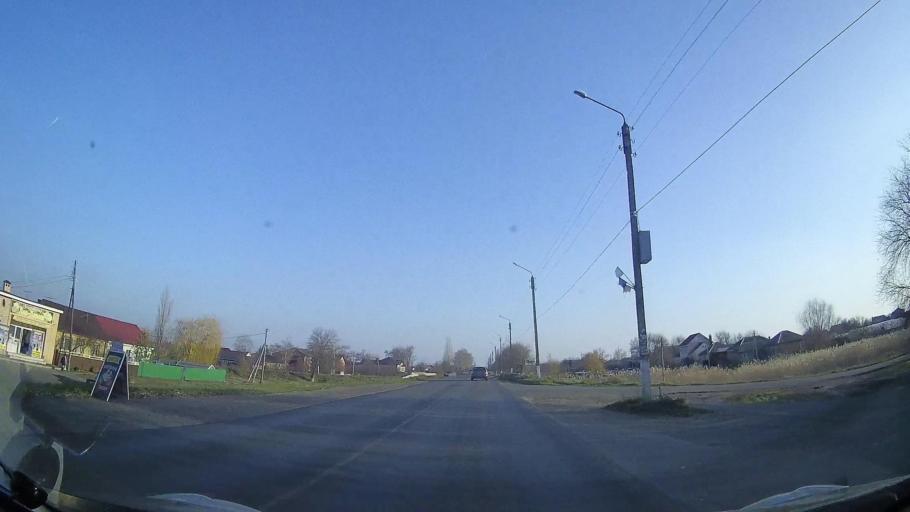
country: RU
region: Rostov
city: Ol'ginskaya
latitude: 47.1863
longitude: 39.9533
